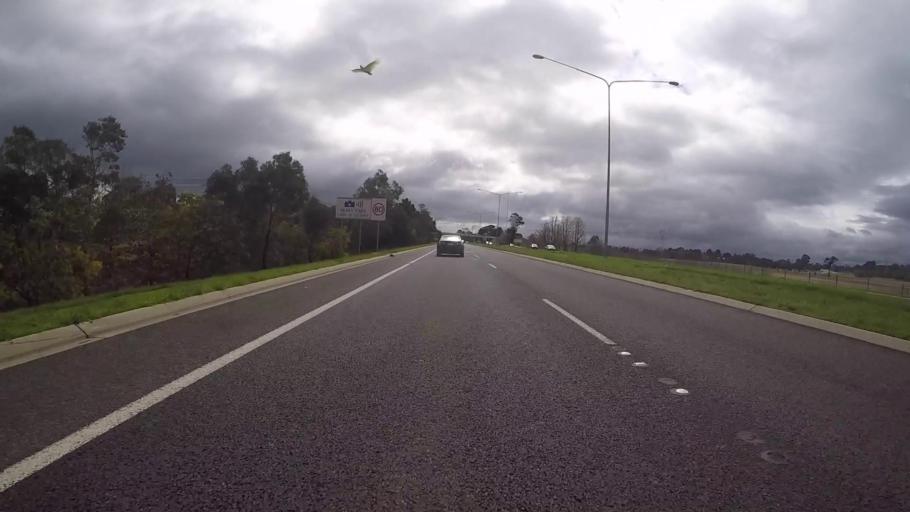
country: AU
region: Australian Capital Territory
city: Kaleen
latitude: -35.2293
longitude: 149.1239
